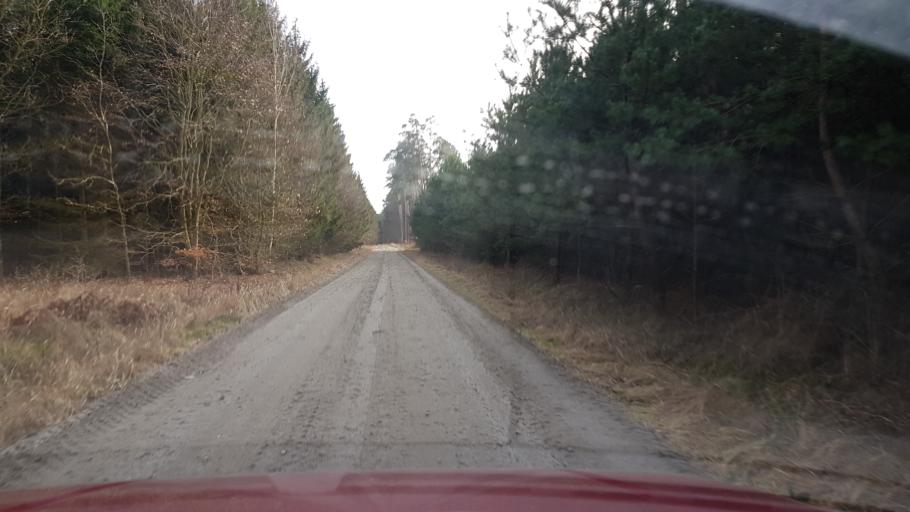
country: PL
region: West Pomeranian Voivodeship
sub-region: Powiat choszczenski
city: Pelczyce
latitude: 52.9256
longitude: 15.3671
